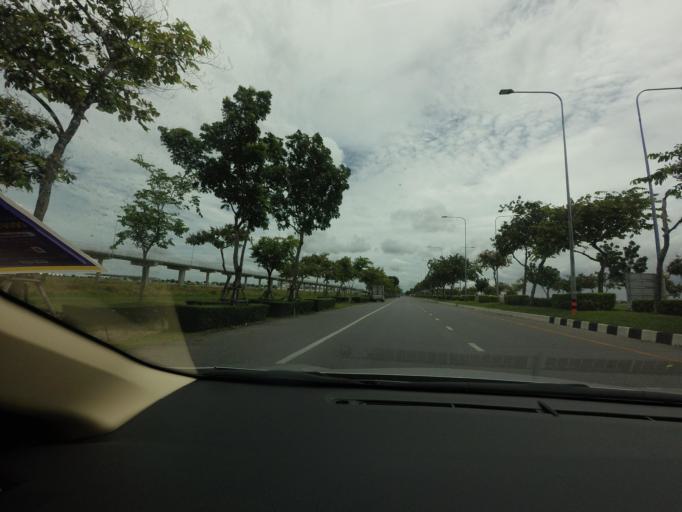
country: TH
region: Bangkok
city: Lat Krabang
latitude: 13.7084
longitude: 100.7739
